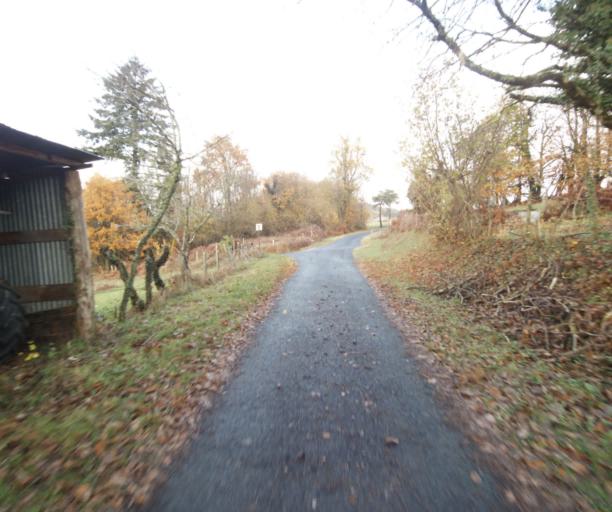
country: FR
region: Limousin
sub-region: Departement de la Correze
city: Cornil
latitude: 45.2205
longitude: 1.6622
